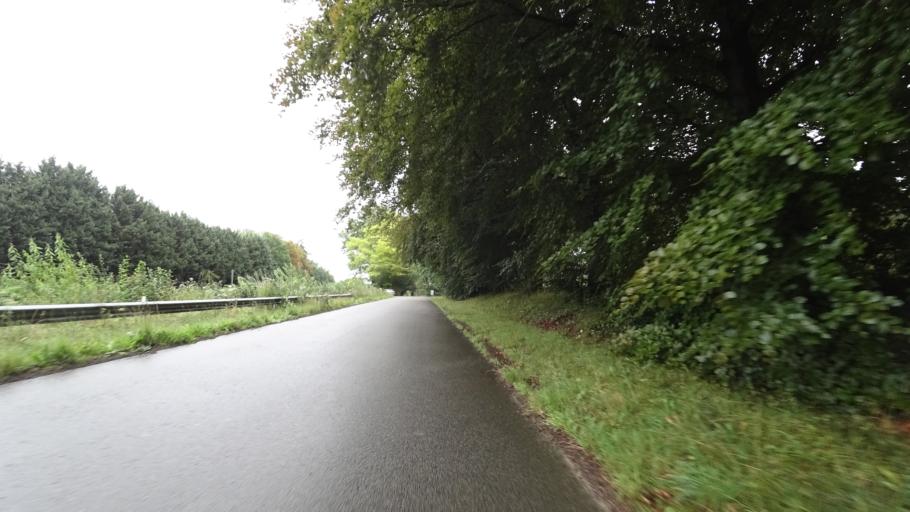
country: BE
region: Wallonia
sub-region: Province de Namur
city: Namur
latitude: 50.4961
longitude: 4.8062
